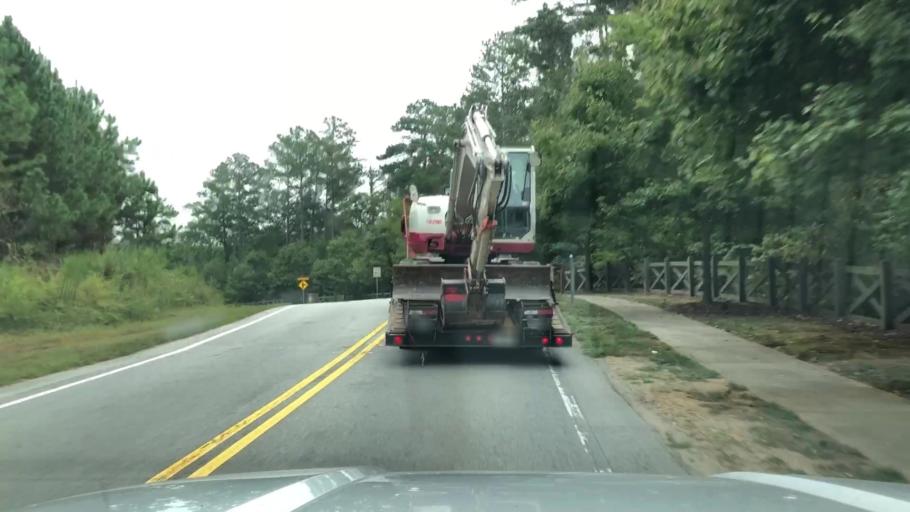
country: US
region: Georgia
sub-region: Bartow County
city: Emerson
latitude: 34.0532
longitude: -84.7928
